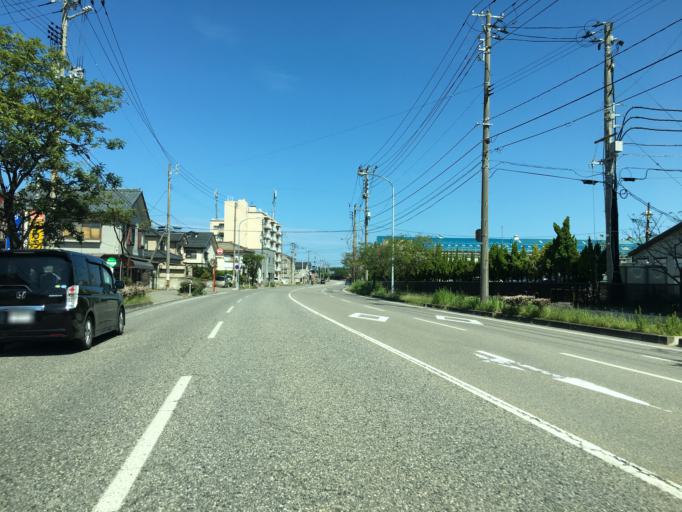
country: JP
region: Niigata
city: Niigata-shi
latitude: 37.9377
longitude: 139.0572
